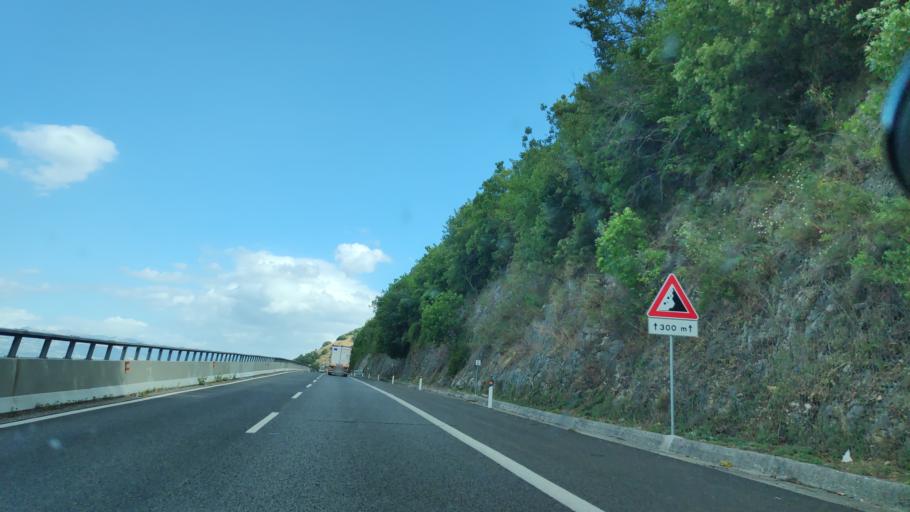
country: IT
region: Campania
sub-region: Provincia di Salerno
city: Sicignano degli Alburni
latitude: 40.5876
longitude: 15.3353
